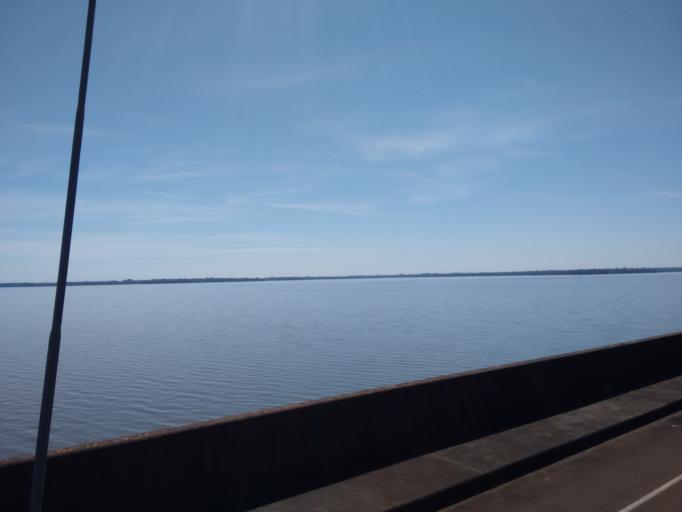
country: PY
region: Alto Parana
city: Ciudad del Este
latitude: -25.4139
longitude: -54.5728
